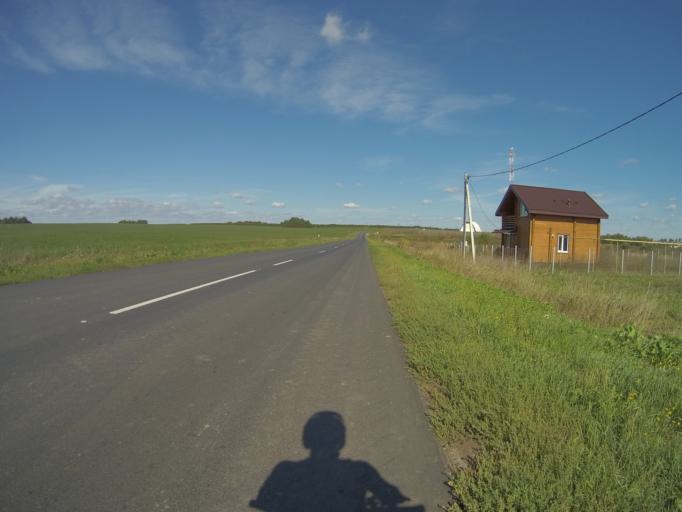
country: RU
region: Vladimir
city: Orgtrud
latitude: 56.3084
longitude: 40.5972
